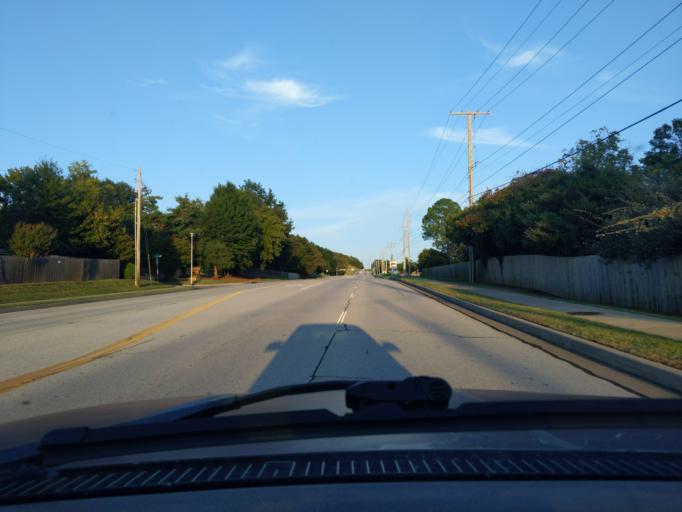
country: US
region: Oklahoma
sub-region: Tulsa County
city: Jenks
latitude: 36.0463
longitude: -95.9441
